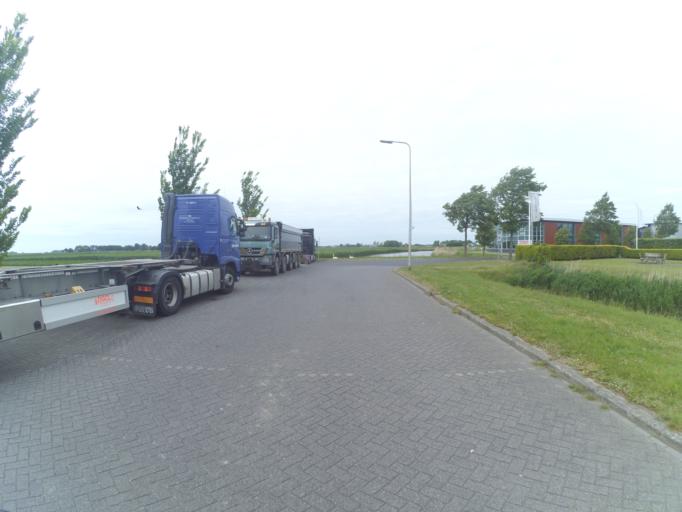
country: NL
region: South Holland
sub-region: Gemeente Spijkenisse
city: Spijkenisse
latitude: 51.8210
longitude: 4.2444
